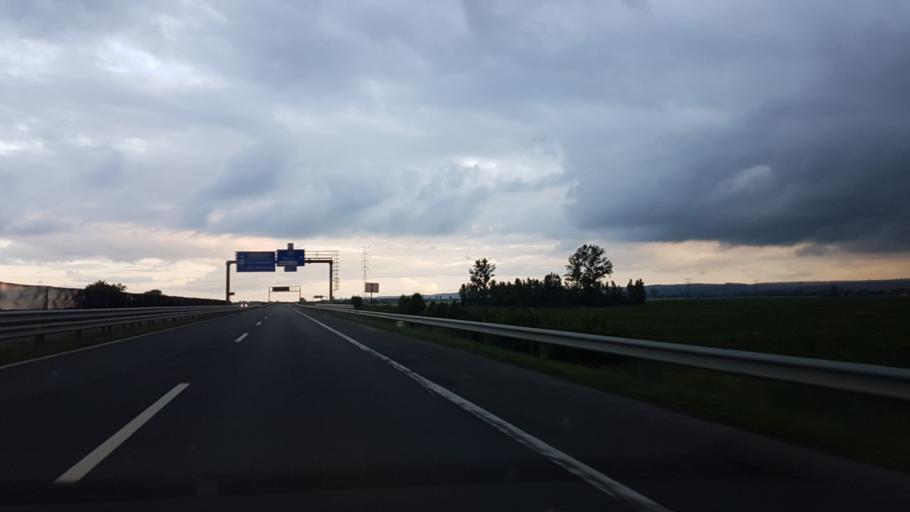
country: HU
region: Borsod-Abauj-Zemplen
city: Felsozsolca
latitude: 48.0753
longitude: 20.8495
